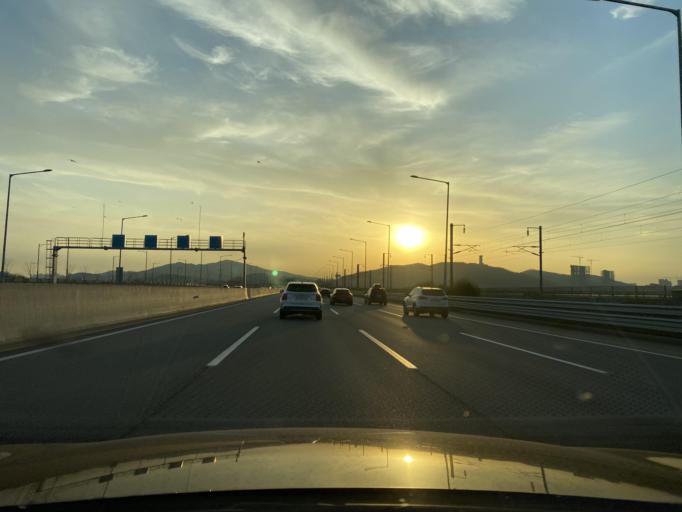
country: KR
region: Gyeonggi-do
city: Tongjin
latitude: 37.5289
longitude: 126.5516
